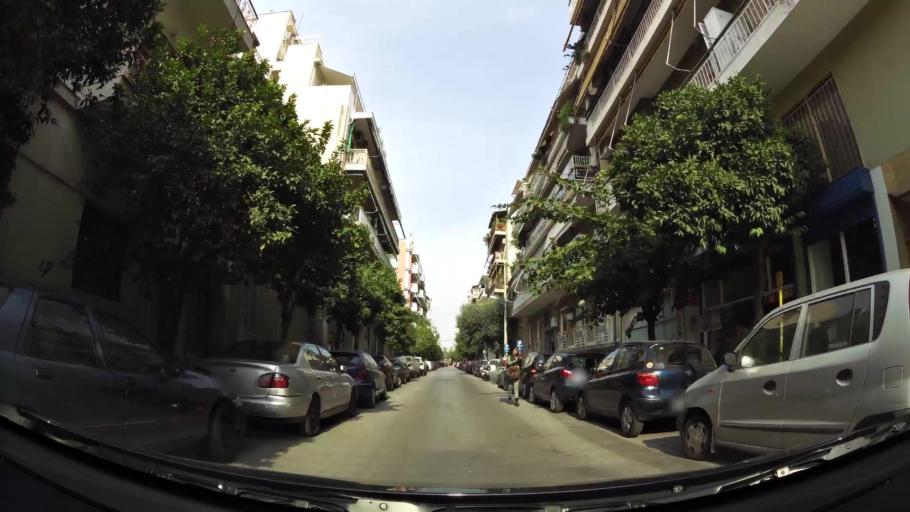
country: GR
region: Attica
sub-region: Nomarchia Athinas
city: Kallithea
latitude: 37.9538
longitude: 23.6958
